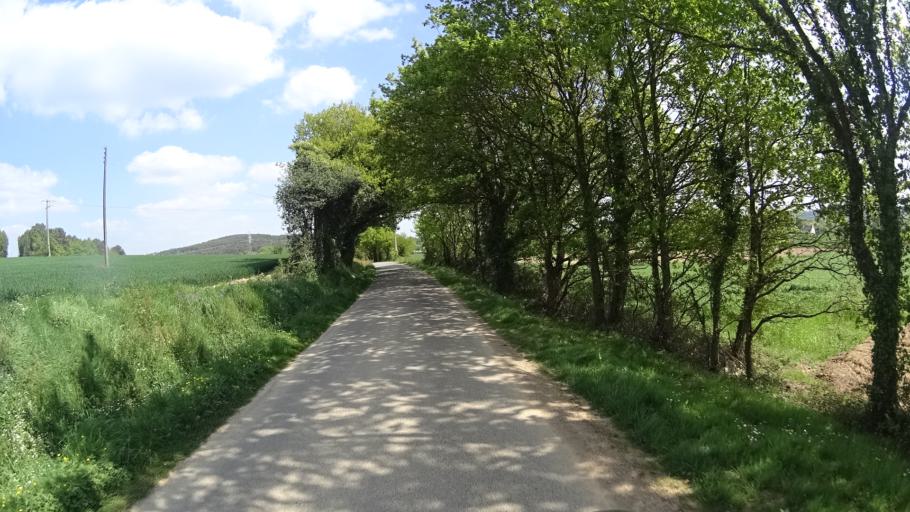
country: FR
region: Brittany
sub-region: Departement du Morbihan
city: Allaire
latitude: 47.5999
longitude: -2.1677
